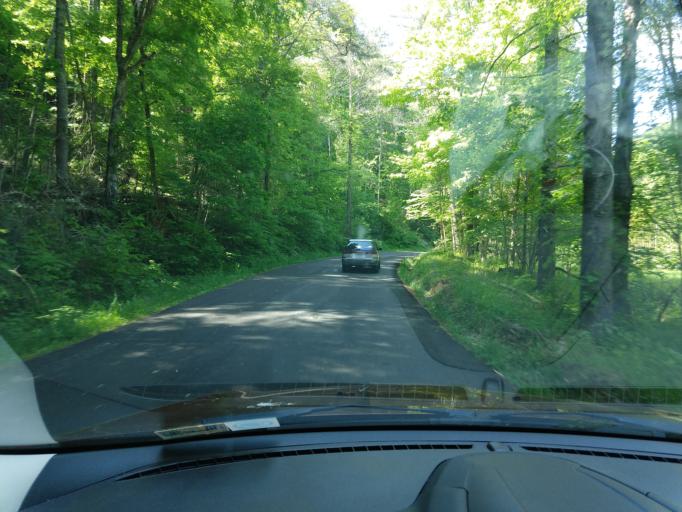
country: US
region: Virginia
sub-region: City of Covington
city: Fairlawn
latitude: 37.6974
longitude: -79.8876
